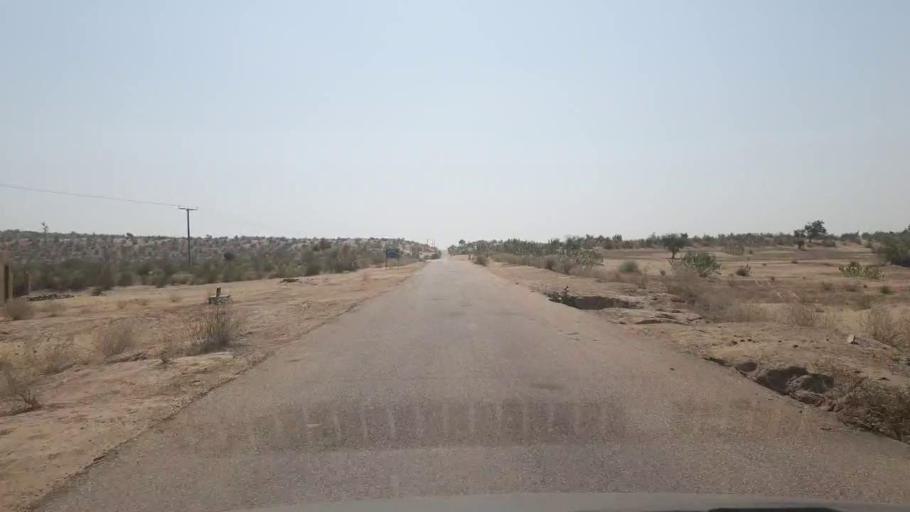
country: PK
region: Sindh
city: Chor
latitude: 25.6363
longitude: 70.1730
